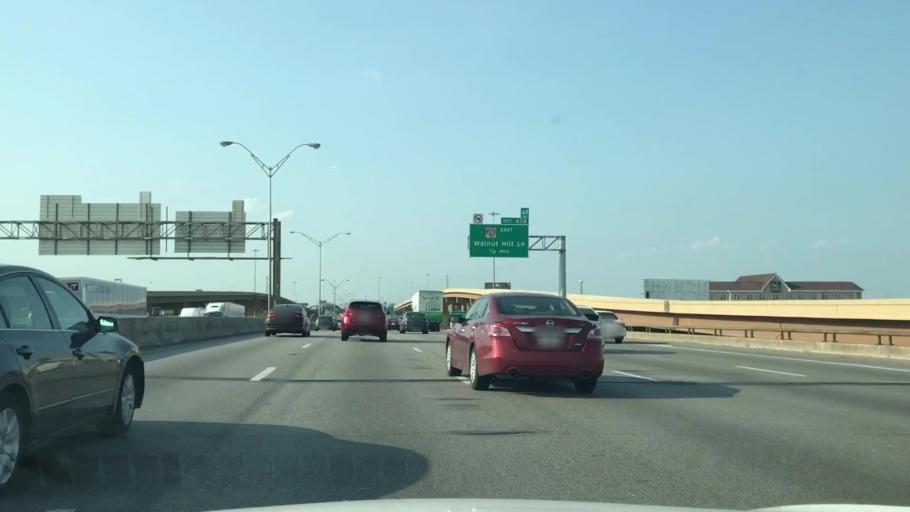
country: US
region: Texas
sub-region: Dallas County
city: Farmers Branch
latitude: 32.8739
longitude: -96.8987
